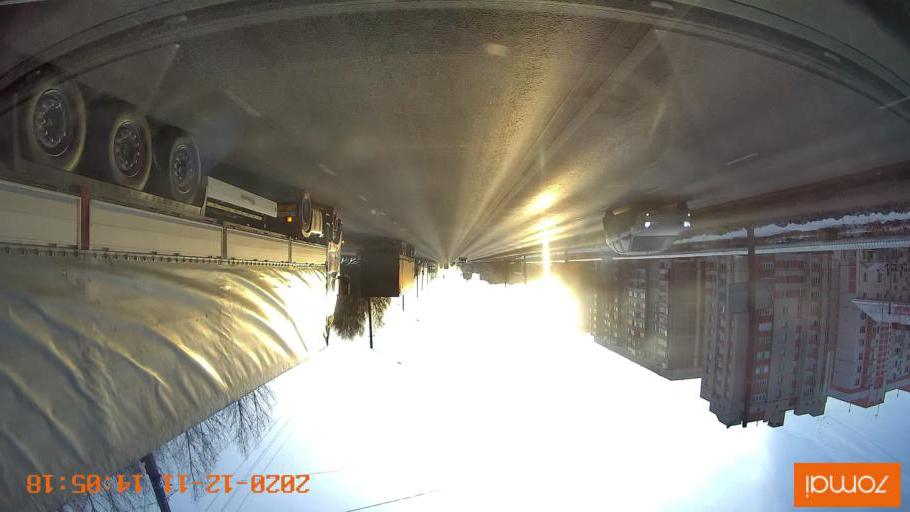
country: RU
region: Kostroma
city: Oktyabr'skiy
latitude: 57.7488
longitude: 41.0142
